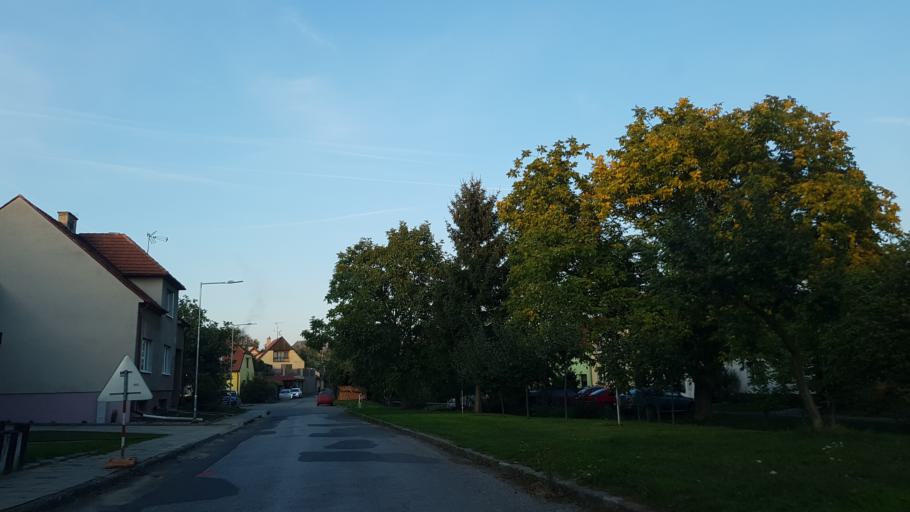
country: CZ
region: Zlin
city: Polesovice
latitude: 49.0285
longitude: 17.3463
